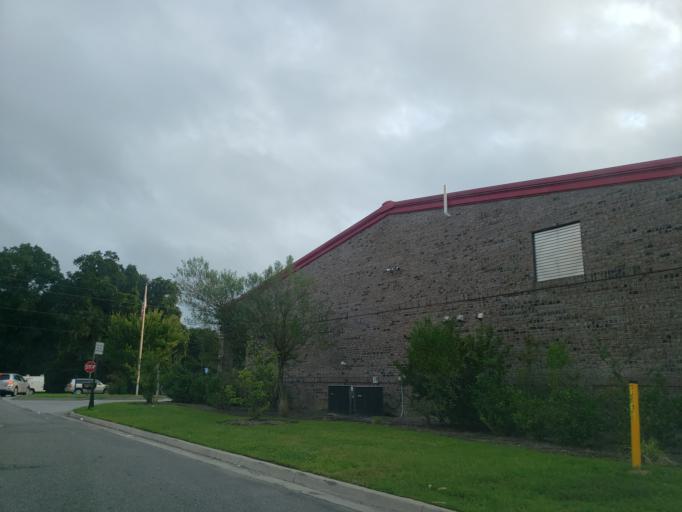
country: US
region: Georgia
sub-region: Chatham County
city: Garden City
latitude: 32.0467
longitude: -81.1693
